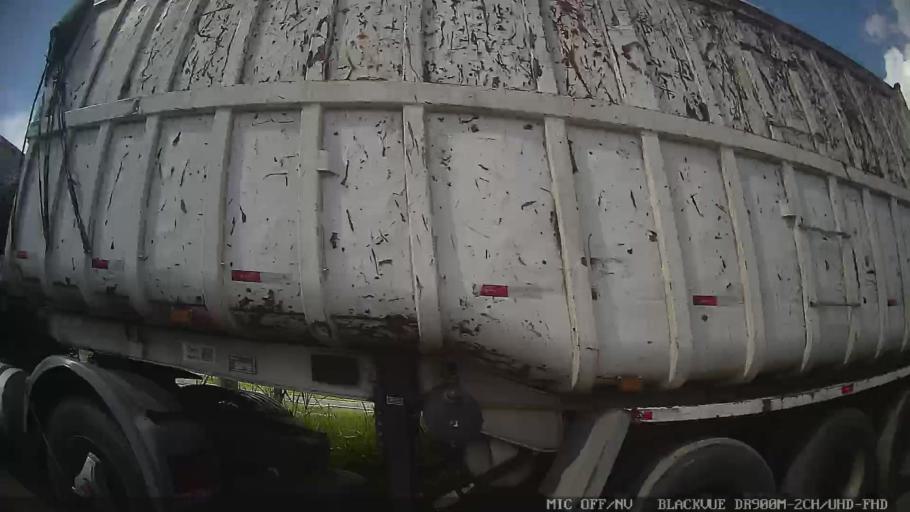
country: BR
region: Sao Paulo
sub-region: Bom Jesus Dos Perdoes
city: Bom Jesus dos Perdoes
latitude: -23.1157
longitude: -46.4864
